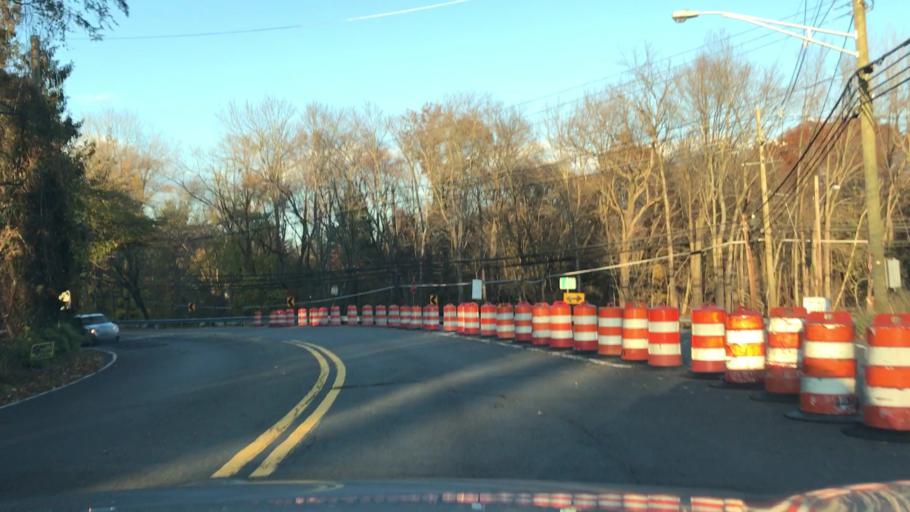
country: US
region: New Jersey
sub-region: Bergen County
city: Harrington Park
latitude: 40.9843
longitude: -73.9753
